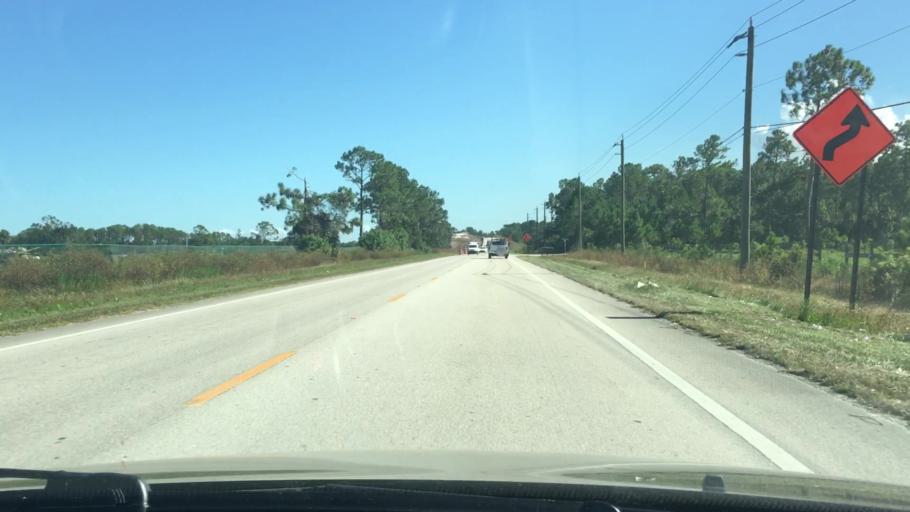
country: US
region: Florida
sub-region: Volusia County
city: South Daytona
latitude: 29.1571
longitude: -81.0843
